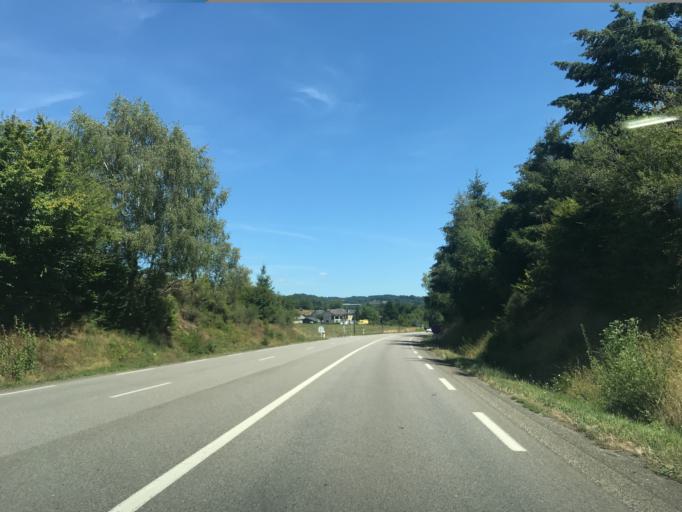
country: FR
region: Limousin
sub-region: Departement de la Correze
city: Tulle
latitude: 45.2879
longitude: 1.8023
